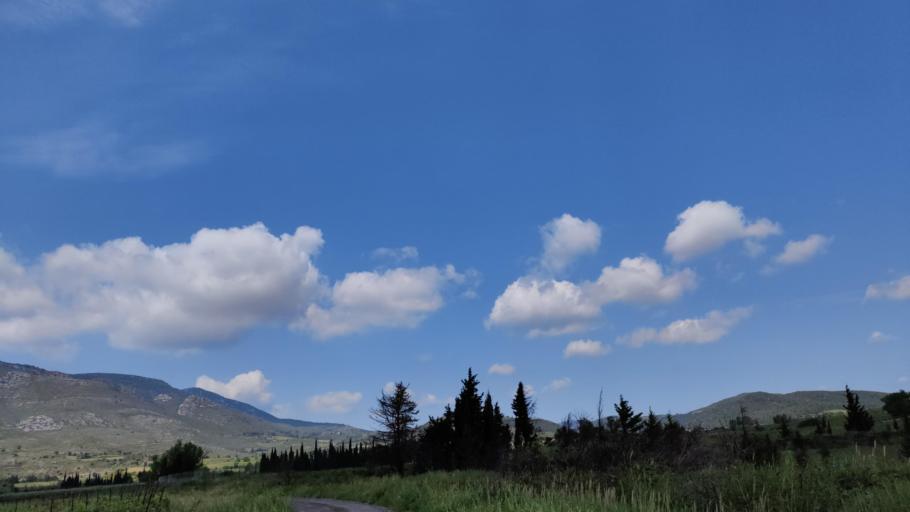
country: FR
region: Languedoc-Roussillon
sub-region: Departement des Pyrenees-Orientales
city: Estagel
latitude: 42.8768
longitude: 2.7211
